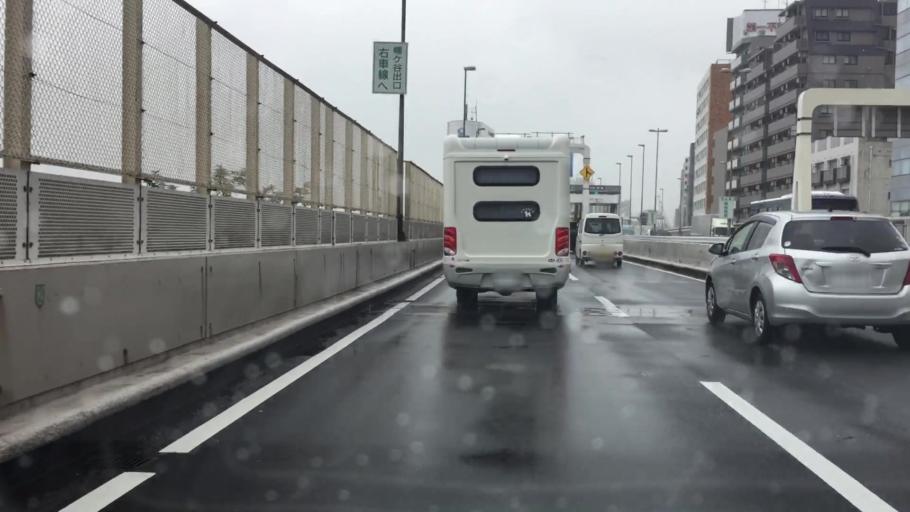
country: JP
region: Tokyo
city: Tokyo
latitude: 35.6777
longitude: 139.6795
